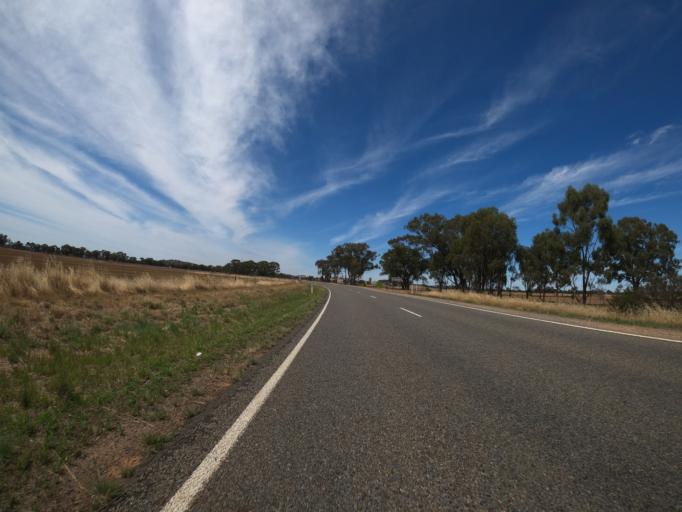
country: AU
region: Victoria
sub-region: Benalla
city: Benalla
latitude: -36.2981
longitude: 145.9524
